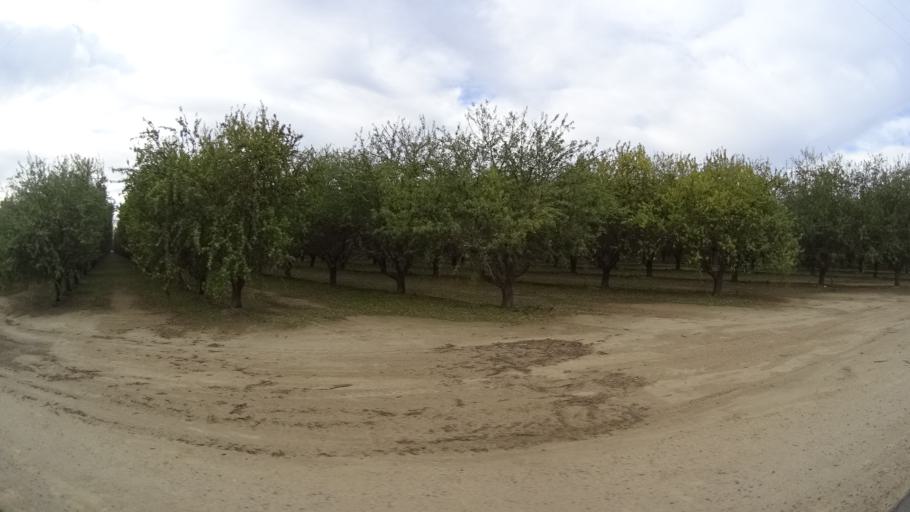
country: US
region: California
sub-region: Kern County
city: Rosedale
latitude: 35.4397
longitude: -119.1968
